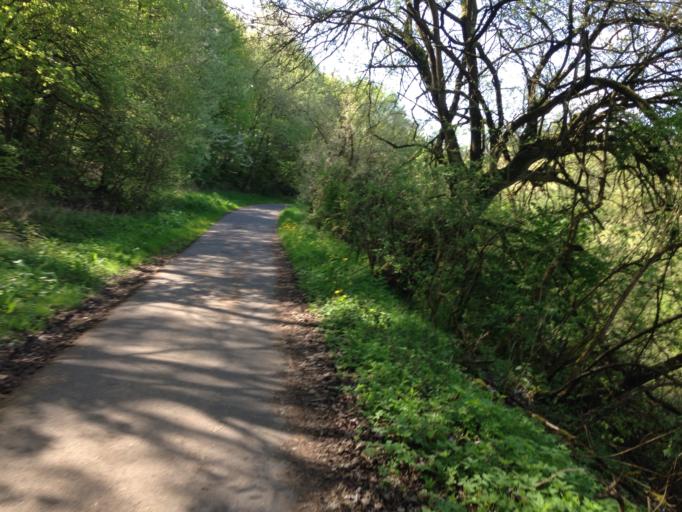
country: DE
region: Hesse
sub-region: Regierungsbezirk Giessen
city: Grunberg
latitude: 50.5475
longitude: 8.9375
